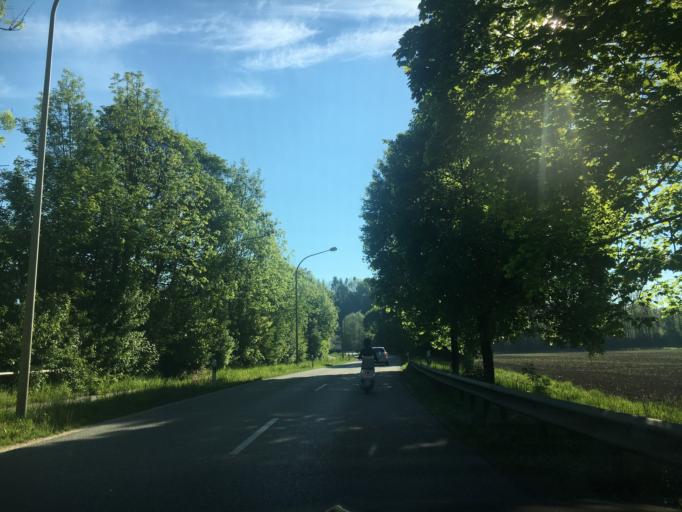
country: DE
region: Bavaria
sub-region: Upper Bavaria
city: Traunreut
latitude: 47.9375
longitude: 12.5969
